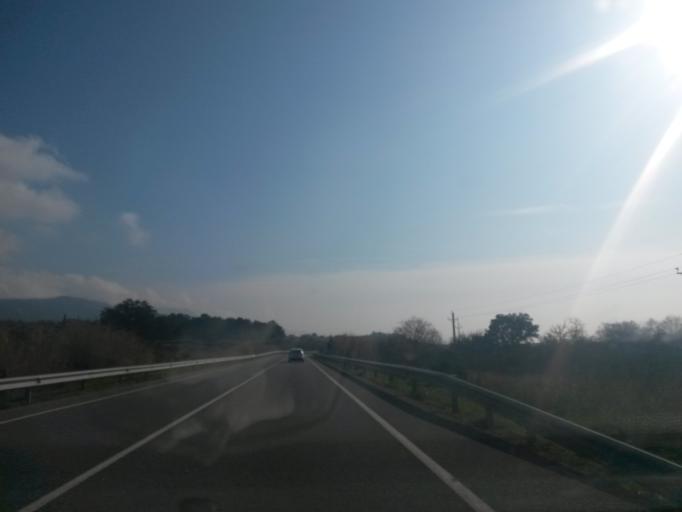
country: ES
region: Catalonia
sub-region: Provincia de Girona
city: Vilajuiga
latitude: 42.3312
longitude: 3.0842
